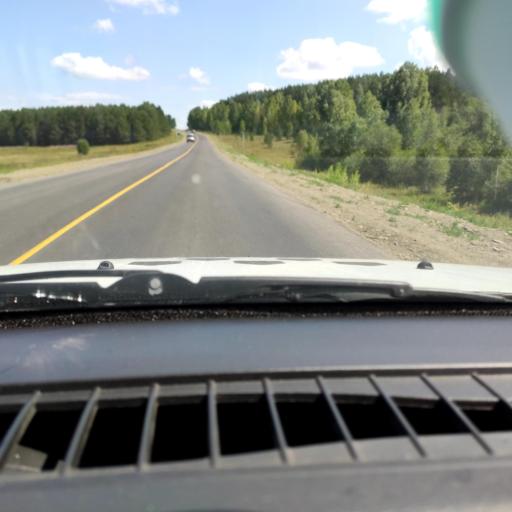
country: RU
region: Bashkortostan
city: Verkhniye Kigi
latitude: 55.3204
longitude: 58.7156
